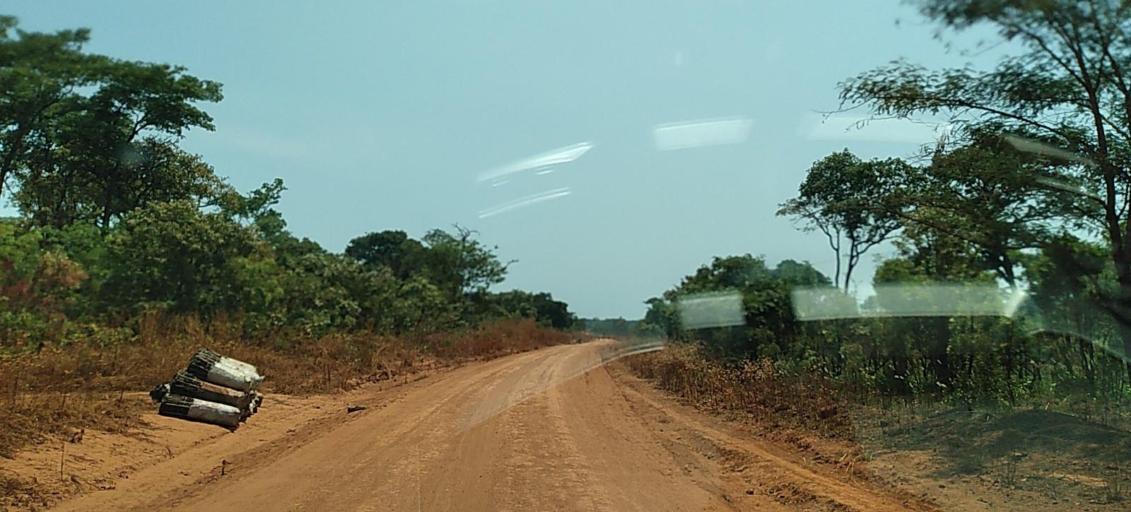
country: CD
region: Katanga
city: Kipushi
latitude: -11.9718
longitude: 26.8966
